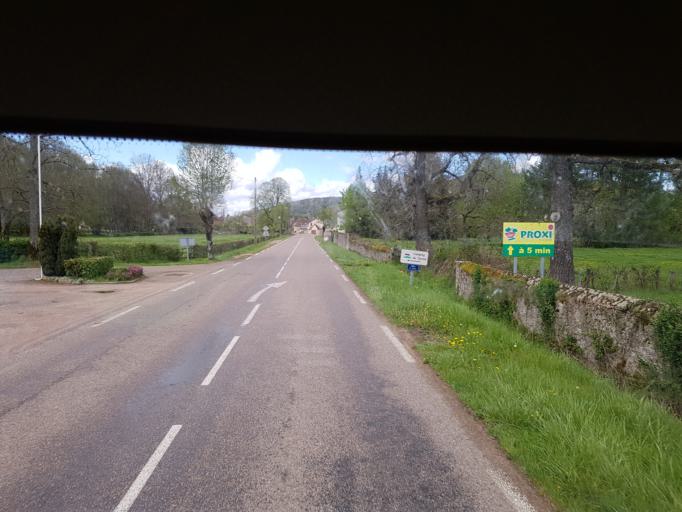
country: FR
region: Bourgogne
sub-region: Departement de Saone-et-Loire
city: Autun
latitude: 47.0763
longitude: 4.2469
